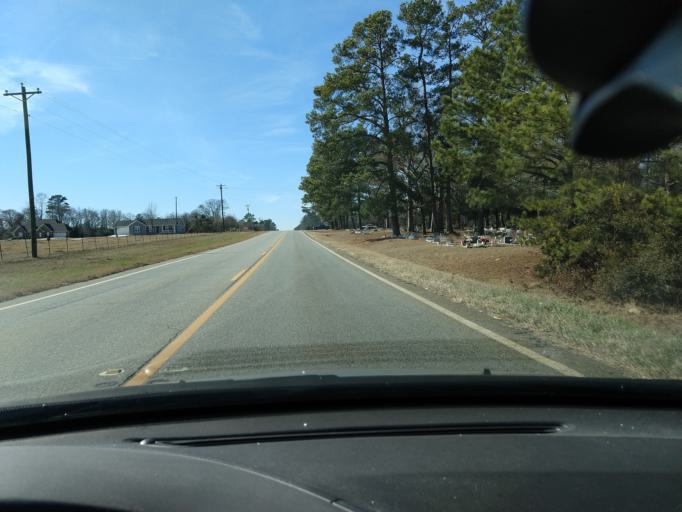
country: US
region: Georgia
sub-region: Dooly County
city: Unadilla
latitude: 32.3404
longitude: -83.7974
